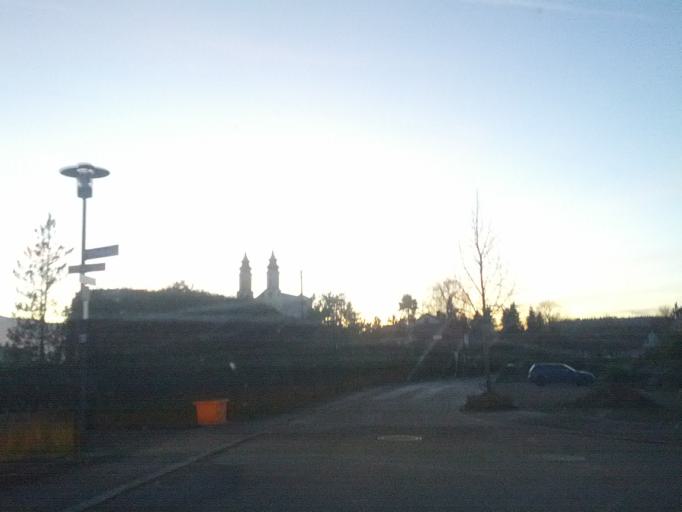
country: DE
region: Baden-Wuerttemberg
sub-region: Tuebingen Region
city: Rot an der Rot
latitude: 48.0161
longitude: 10.0344
